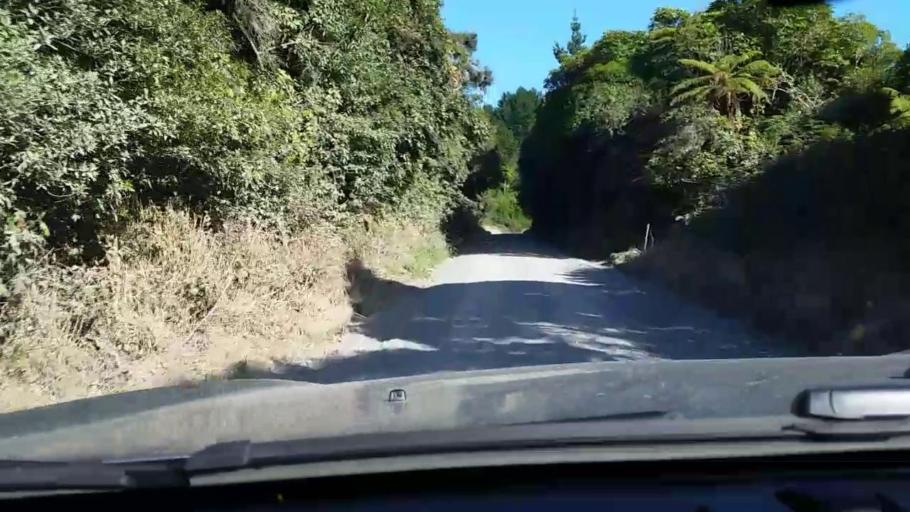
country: NZ
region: Waikato
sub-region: Taupo District
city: Taupo
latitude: -38.4741
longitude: 176.1677
